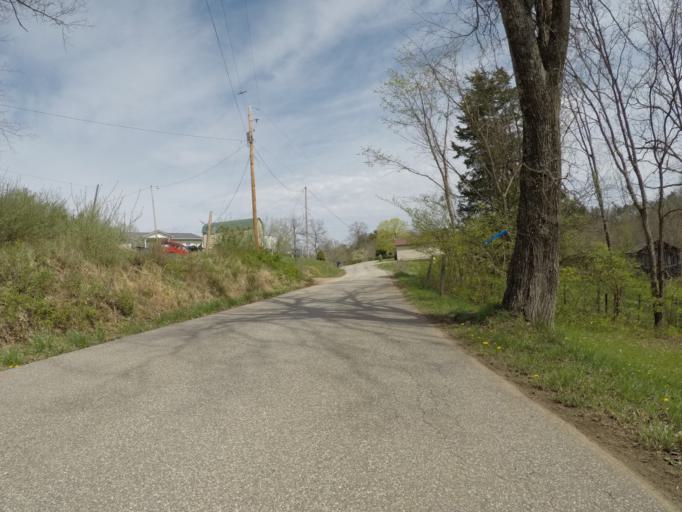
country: US
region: West Virginia
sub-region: Cabell County
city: Pea Ridge
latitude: 38.3395
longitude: -82.3619
